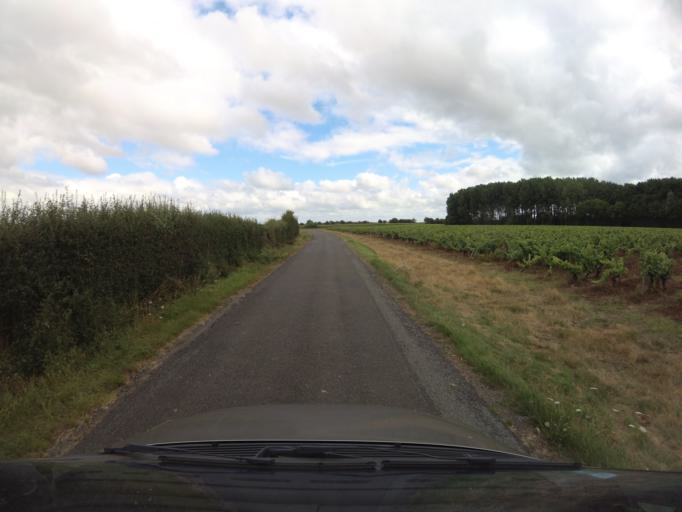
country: FR
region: Pays de la Loire
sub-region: Departement de la Vendee
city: Saint-Philbert-de-Bouaine
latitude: 47.0037
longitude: -1.5286
